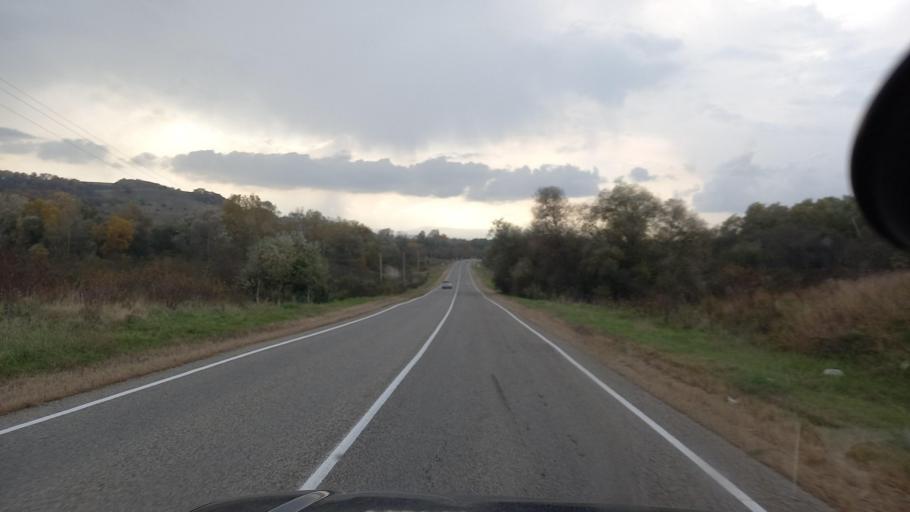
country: RU
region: Krasnodarskiy
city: Perepravnaya
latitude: 44.3748
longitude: 40.7340
